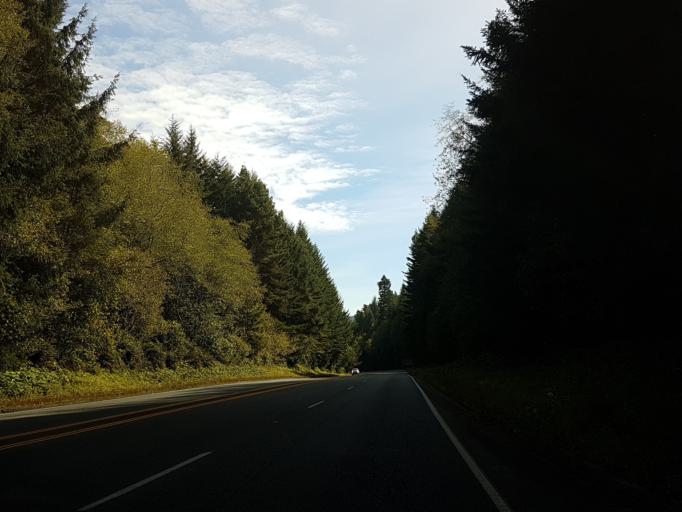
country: US
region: California
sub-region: Del Norte County
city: Bertsch-Oceanview
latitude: 41.4798
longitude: -124.0486
